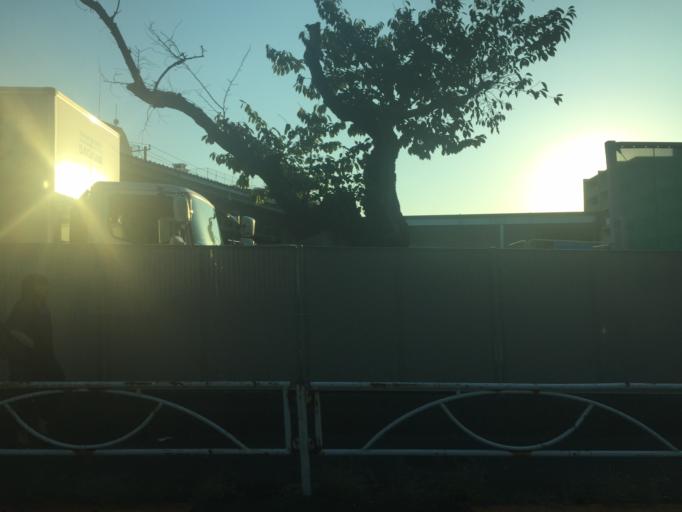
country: JP
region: Tokyo
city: Tokyo
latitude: 35.6235
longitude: 139.6385
